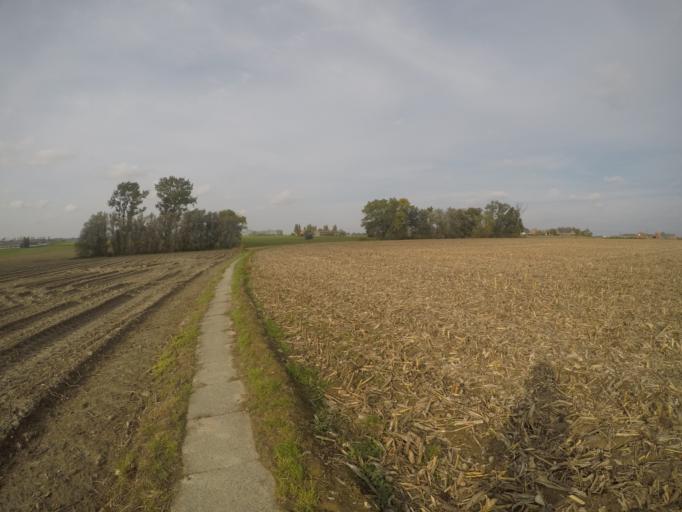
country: BE
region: Flanders
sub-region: Provincie West-Vlaanderen
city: Wervik
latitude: 50.8339
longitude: 3.0582
